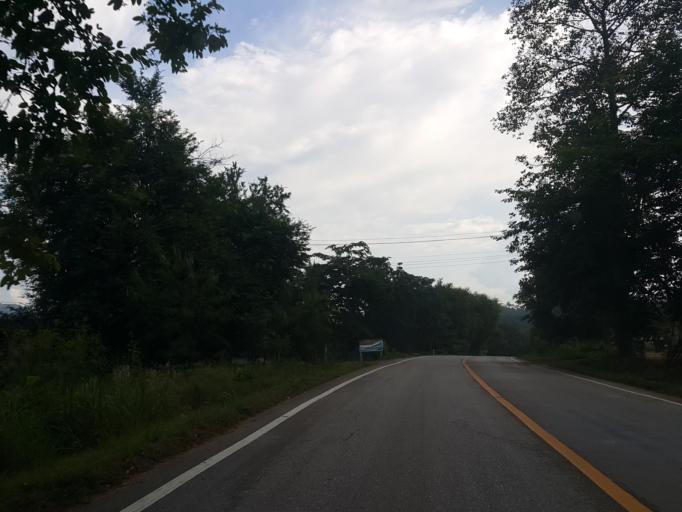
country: TH
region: Chiang Mai
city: Phrao
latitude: 19.2755
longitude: 99.1893
